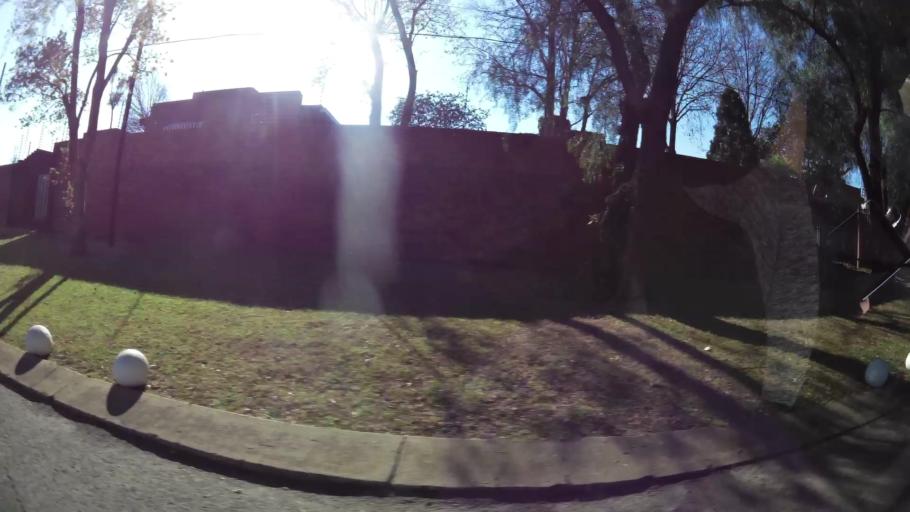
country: ZA
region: Gauteng
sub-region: City of Johannesburg Metropolitan Municipality
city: Midrand
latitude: -26.0485
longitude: 28.0507
